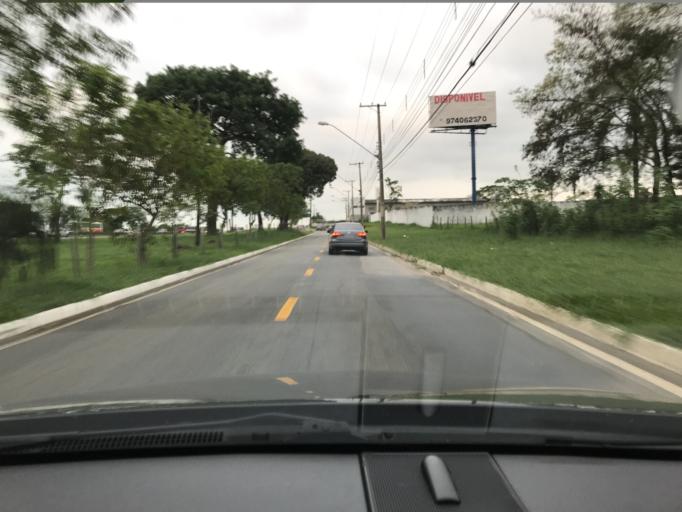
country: BR
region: Sao Paulo
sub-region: Cacapava
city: Cacapava
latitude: -23.1534
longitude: -45.7871
